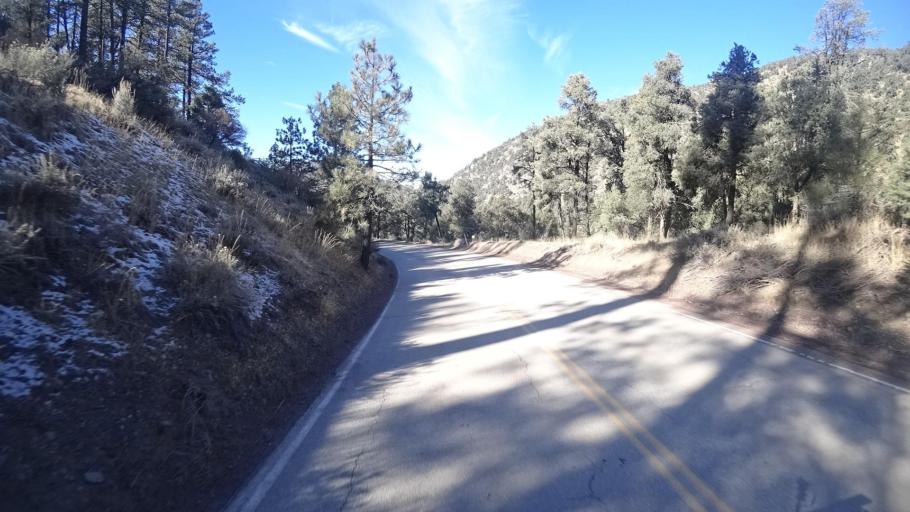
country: US
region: California
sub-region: Kern County
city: Pine Mountain Club
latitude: 34.8502
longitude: -119.1066
